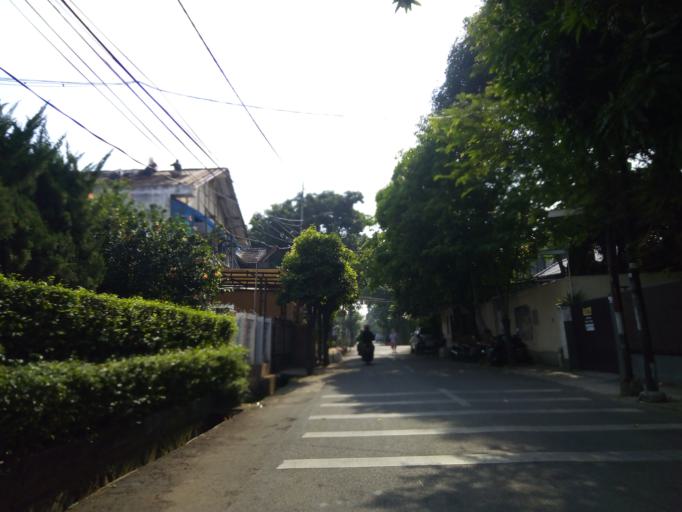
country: ID
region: Jakarta Raya
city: Jakarta
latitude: -6.2096
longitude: 106.8352
